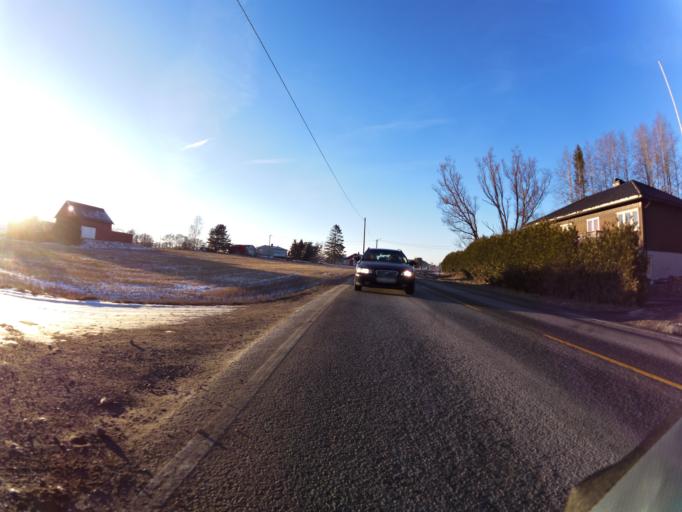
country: NO
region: Ostfold
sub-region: Fredrikstad
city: Fredrikstad
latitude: 59.2525
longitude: 10.8472
